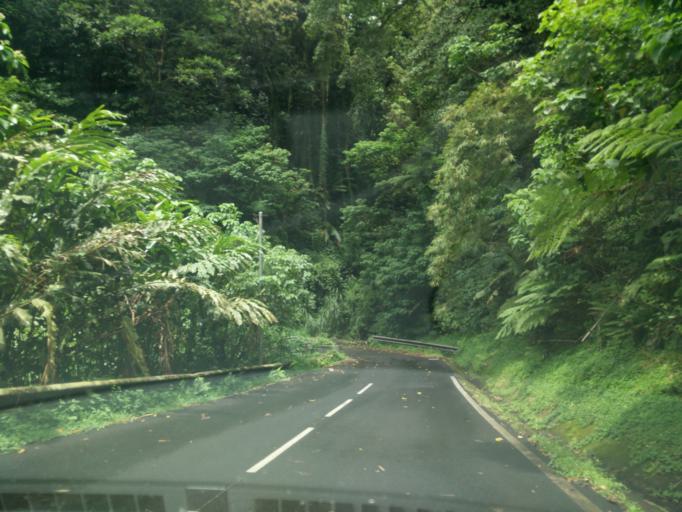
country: MQ
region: Martinique
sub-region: Martinique
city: Le Morne-Rouge
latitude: 14.7292
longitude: -61.1175
